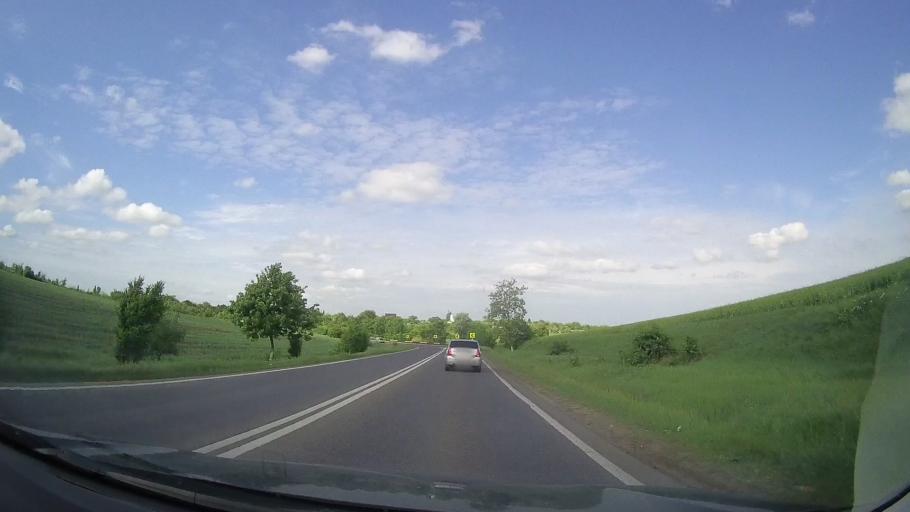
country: RO
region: Giurgiu
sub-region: Comuna Bulbucata
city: Bulbucata
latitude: 44.2439
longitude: 25.8246
